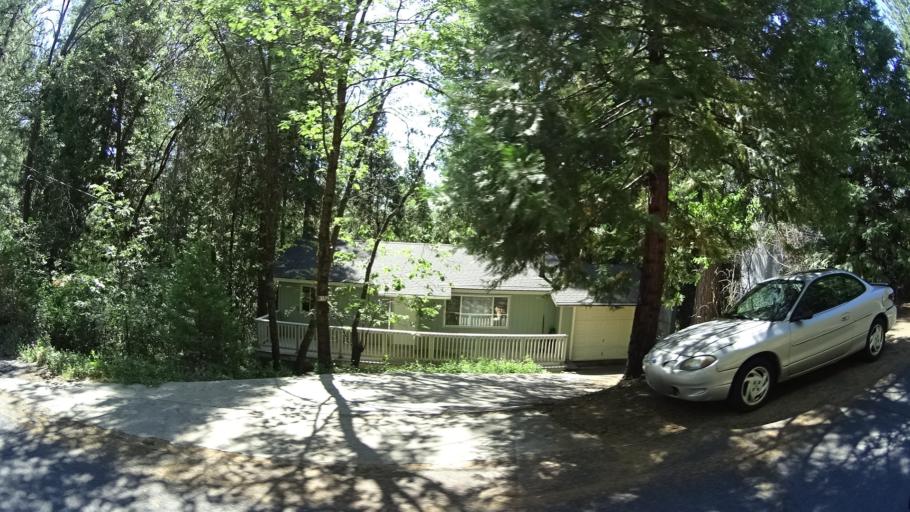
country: US
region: California
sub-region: Calaveras County
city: Arnold
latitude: 38.2403
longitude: -120.3716
